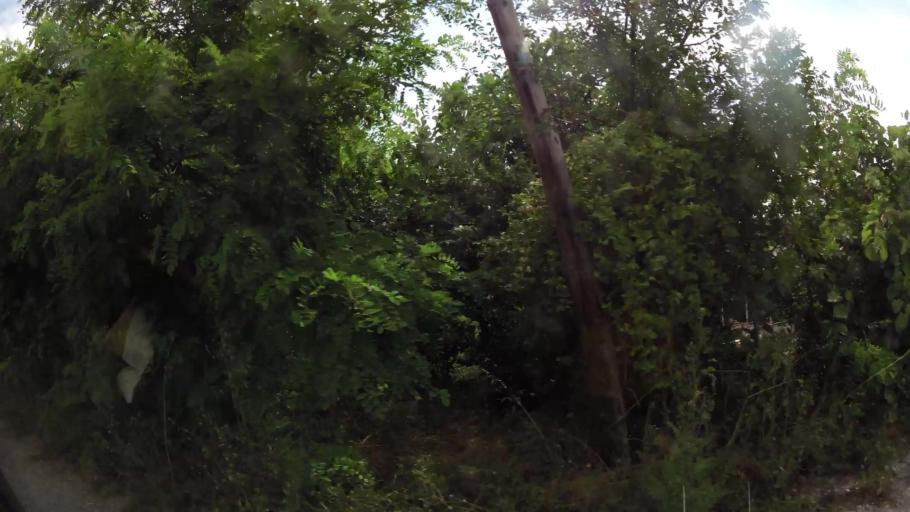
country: GR
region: Central Macedonia
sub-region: Nomos Pierias
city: Makrygialos
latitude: 40.4206
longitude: 22.6067
